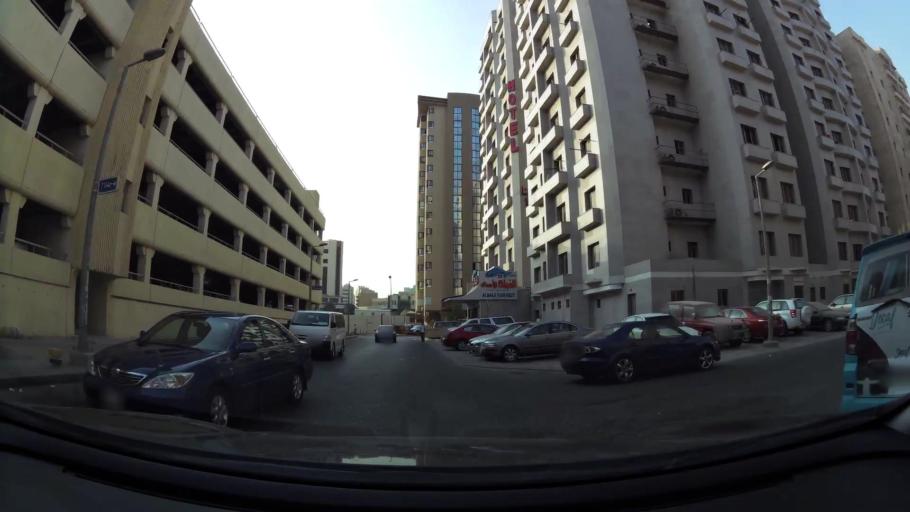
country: KW
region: Muhafazat Hawalli
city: As Salimiyah
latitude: 29.3353
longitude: 48.0590
